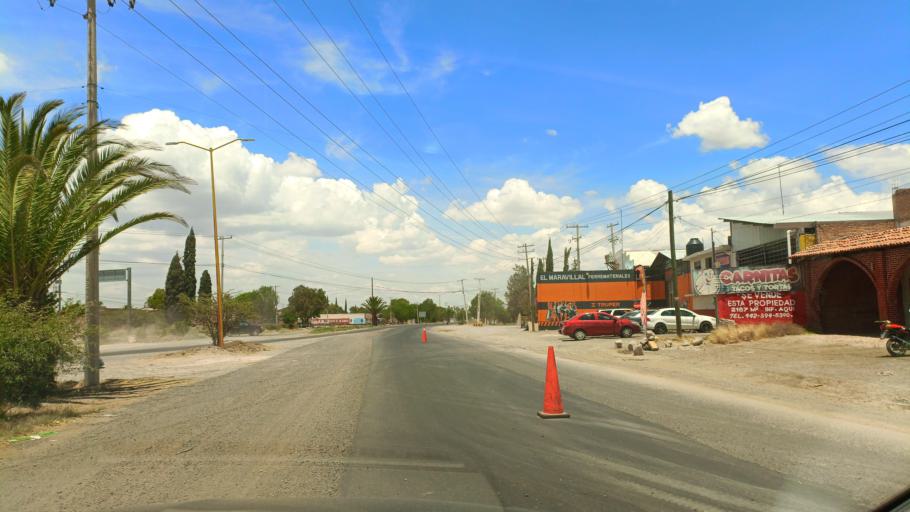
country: MX
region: Guanajuato
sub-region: San Luis de la Paz
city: San Ignacio
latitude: 21.2879
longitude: -100.5562
